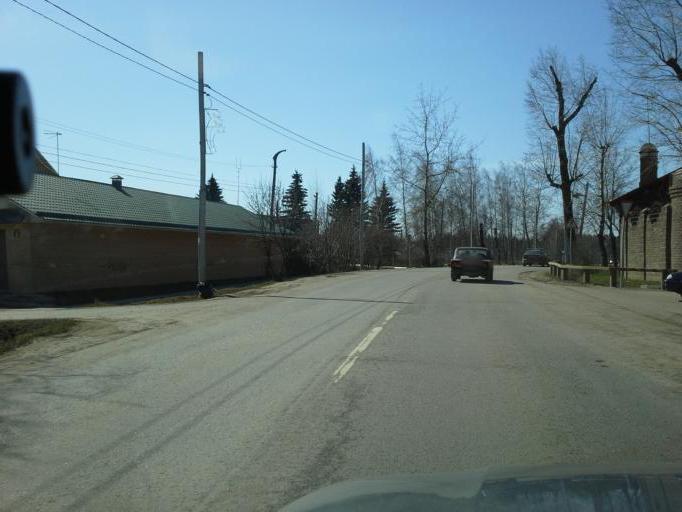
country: RU
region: Moskovskaya
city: Odintsovo
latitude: 55.6456
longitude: 37.2688
